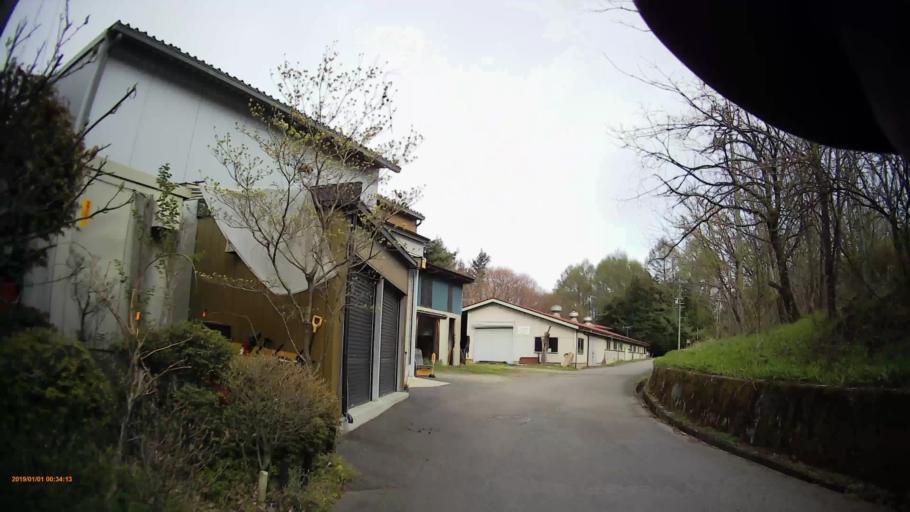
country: JP
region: Nagano
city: Chino
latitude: 35.9331
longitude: 138.2032
